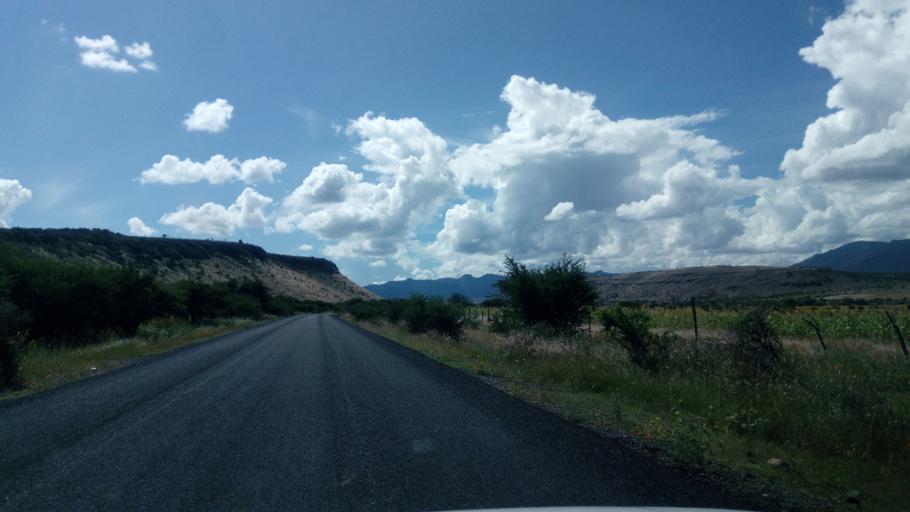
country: MX
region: Durango
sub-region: Durango
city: Jose Refugio Salcido
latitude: 23.8406
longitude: -104.4808
